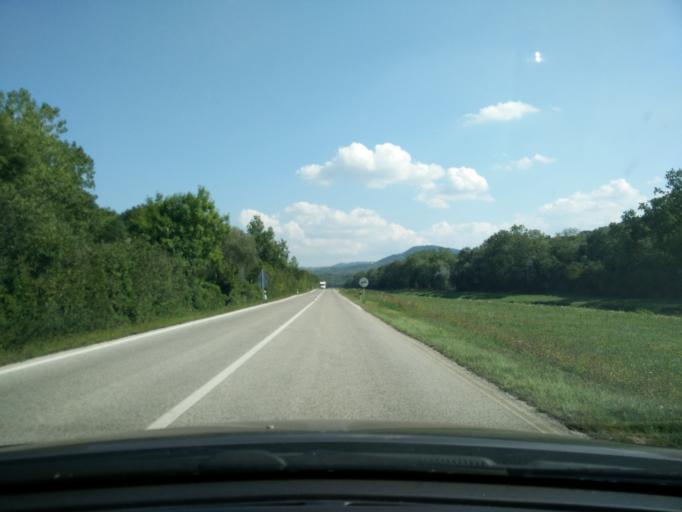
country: HR
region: Istarska
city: Karojba
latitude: 45.3501
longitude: 13.7742
